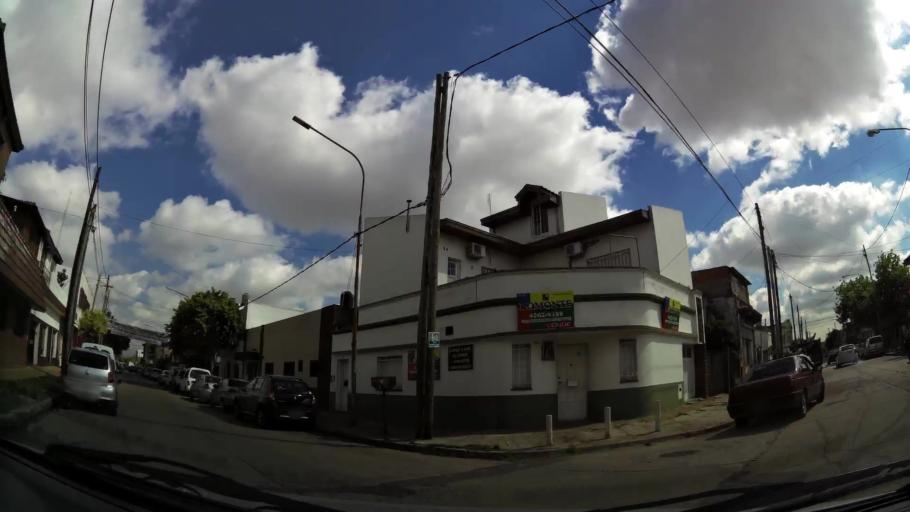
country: AR
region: Buenos Aires
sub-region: Partido de Lanus
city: Lanus
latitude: -34.6903
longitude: -58.4055
